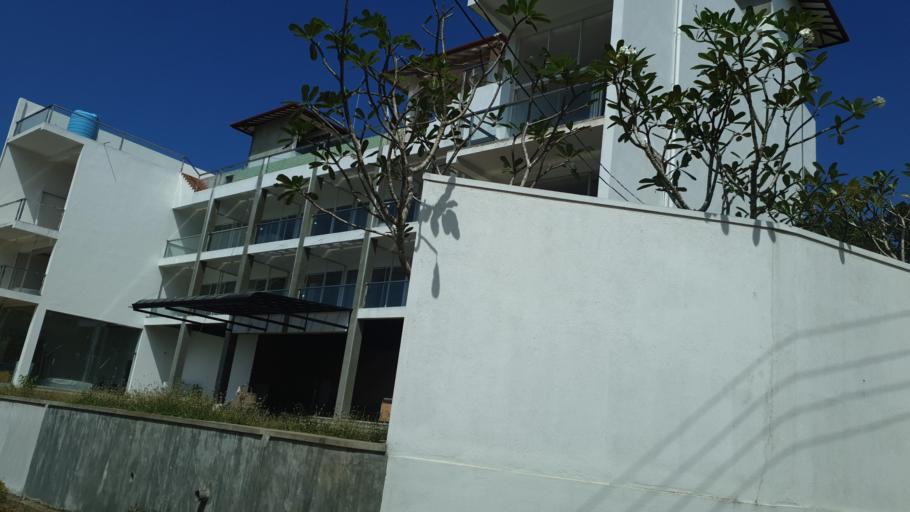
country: LK
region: Southern
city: Tangalla
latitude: 5.9617
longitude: 80.7139
